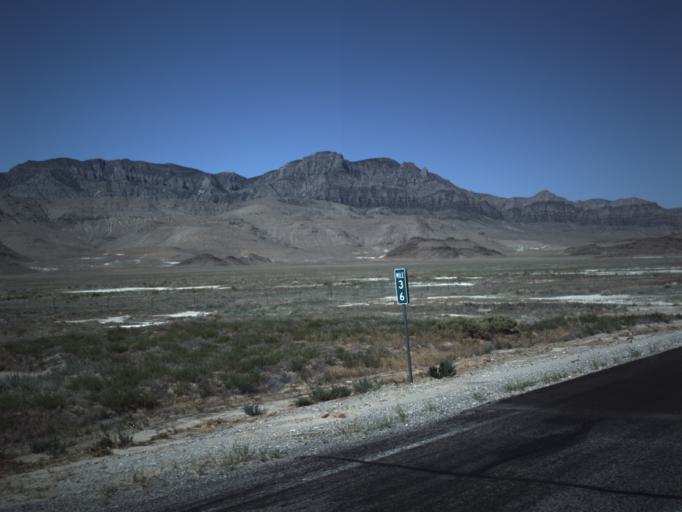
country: US
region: Utah
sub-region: Beaver County
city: Milford
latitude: 39.0476
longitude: -113.4139
